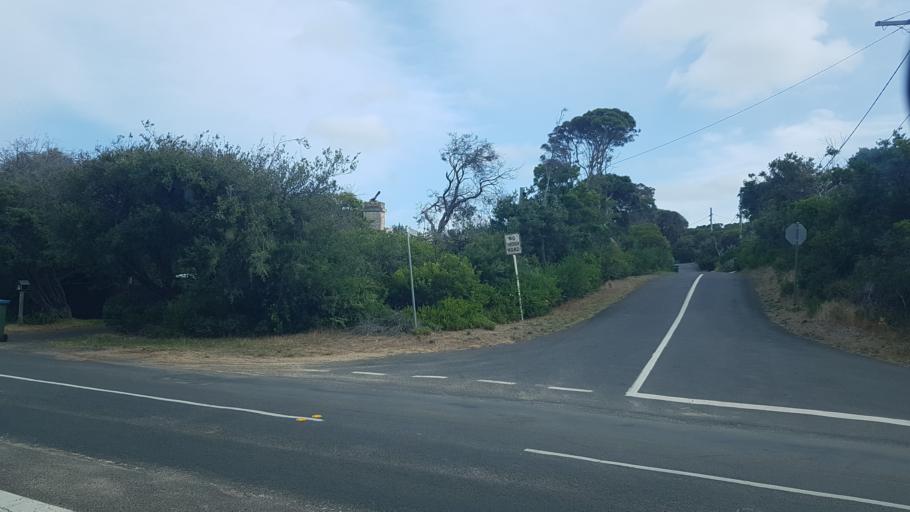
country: AU
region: Victoria
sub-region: Mornington Peninsula
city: Sorrento
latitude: -38.3293
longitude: 144.7074
